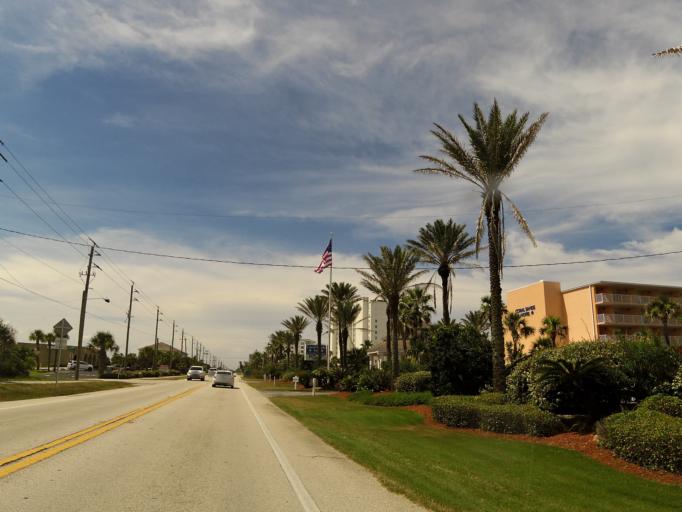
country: US
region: Florida
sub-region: Volusia County
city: Ormond Beach
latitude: 29.3157
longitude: -81.0516
